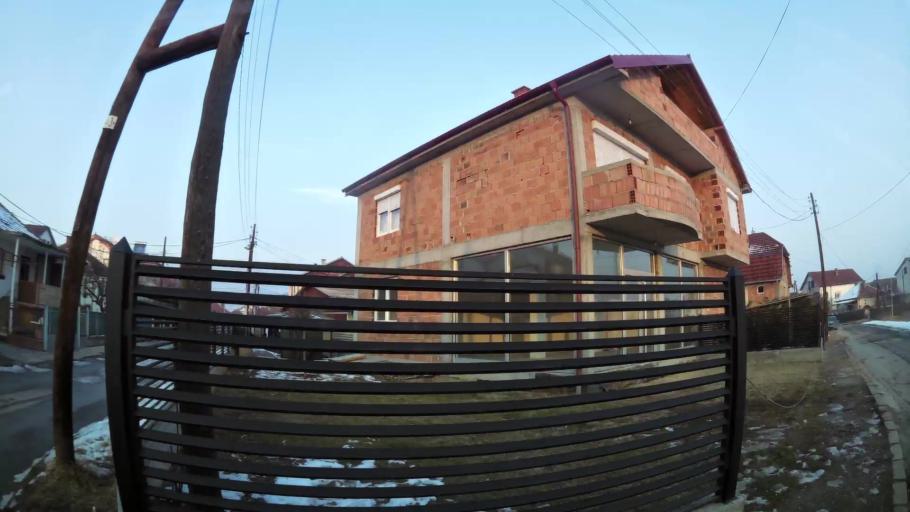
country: MK
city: Creshevo
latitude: 42.0131
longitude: 21.5114
